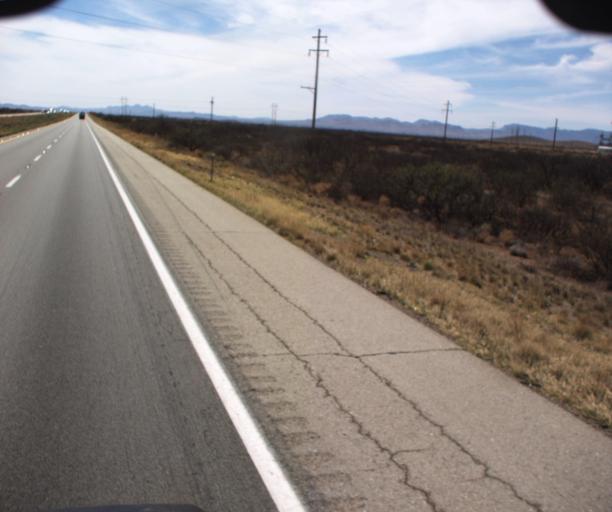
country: US
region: Arizona
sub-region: Cochise County
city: Willcox
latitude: 32.3405
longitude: -109.7560
